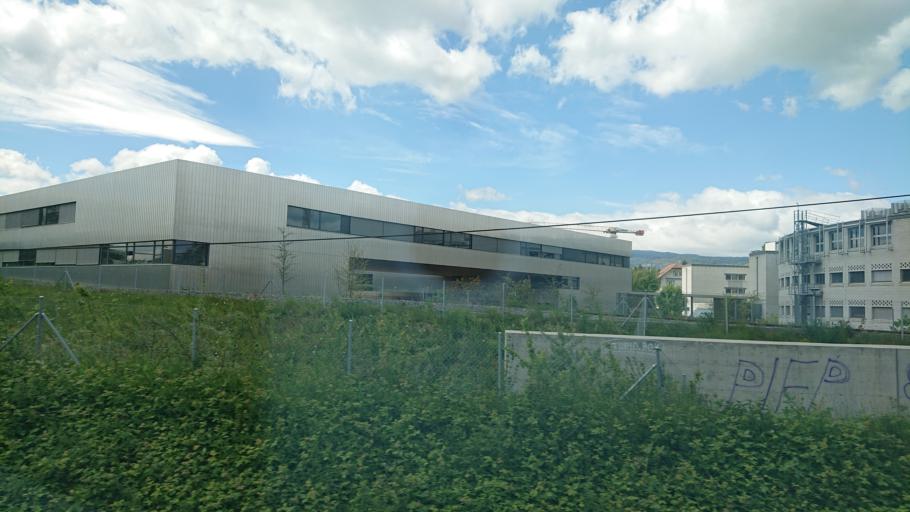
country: CH
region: Vaud
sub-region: Nyon District
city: Nyon
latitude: 46.3816
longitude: 6.2325
